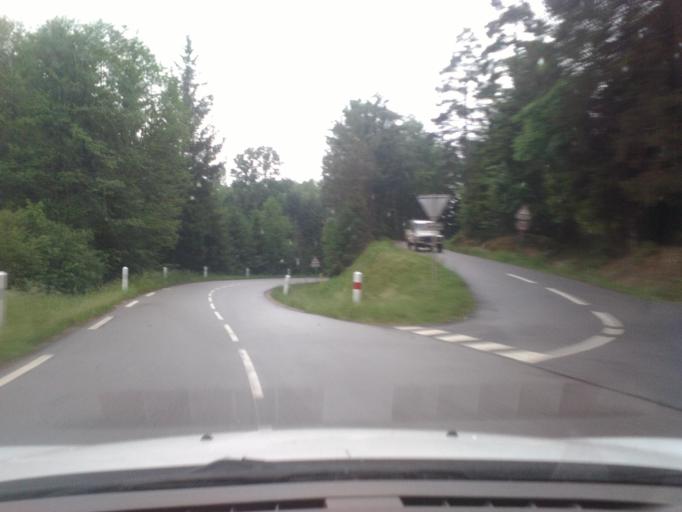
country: FR
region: Lorraine
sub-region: Departement des Vosges
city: Bruyeres
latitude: 48.2526
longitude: 6.7293
